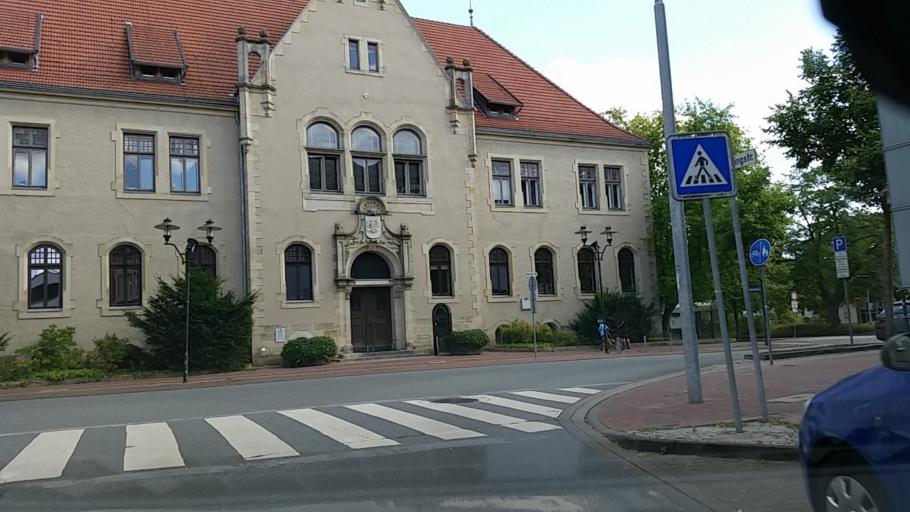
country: DE
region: Lower Saxony
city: Uelzen
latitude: 52.9631
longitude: 10.5580
